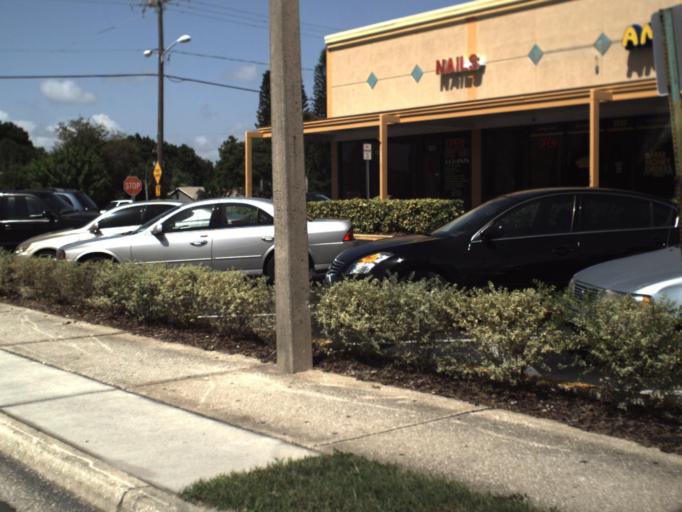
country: US
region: Florida
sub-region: Pinellas County
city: Clearwater
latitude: 27.9531
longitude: -82.7875
